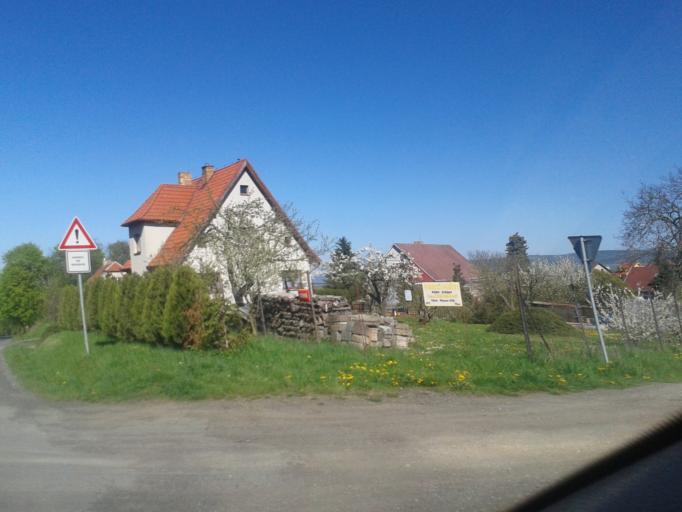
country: CZ
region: Central Bohemia
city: Revnice
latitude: 49.8986
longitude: 14.1432
